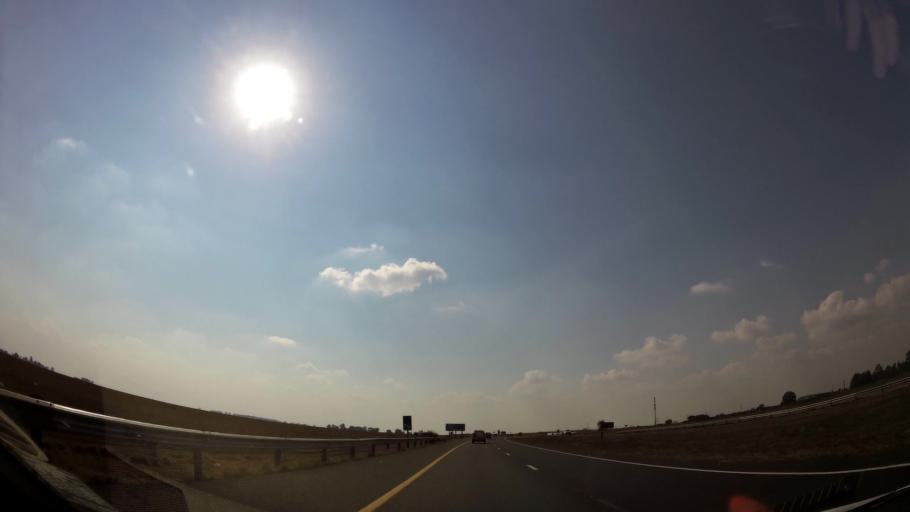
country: ZA
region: Mpumalanga
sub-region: Nkangala District Municipality
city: Delmas
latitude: -26.1512
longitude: 28.5279
